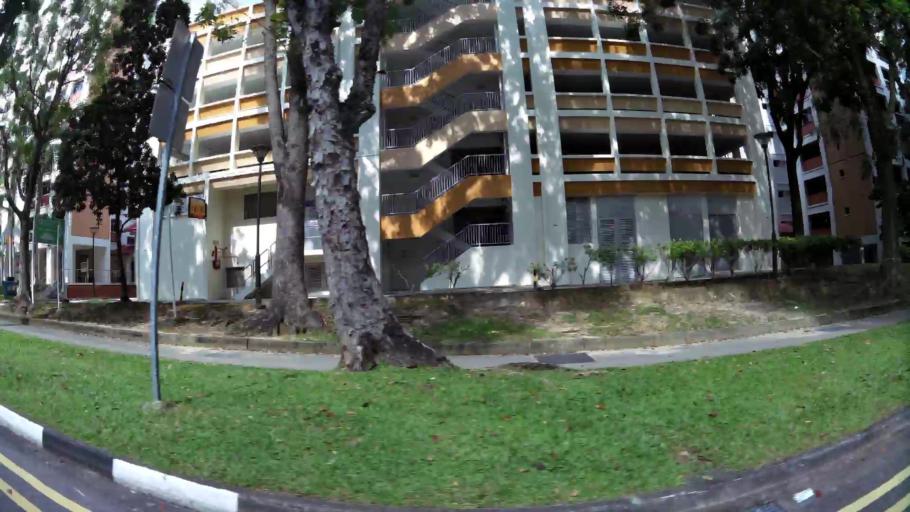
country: SG
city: Singapore
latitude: 1.3508
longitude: 103.8885
